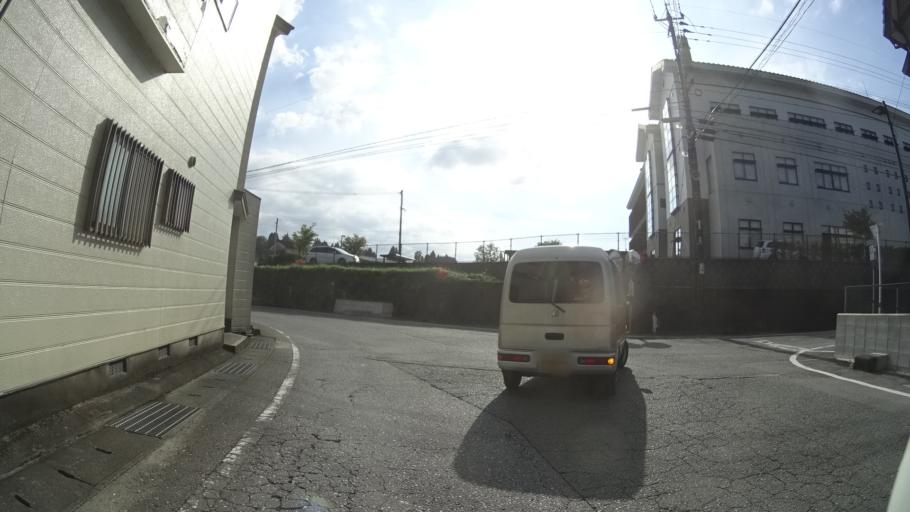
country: JP
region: Kumamoto
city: Ozu
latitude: 32.6853
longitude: 130.9910
